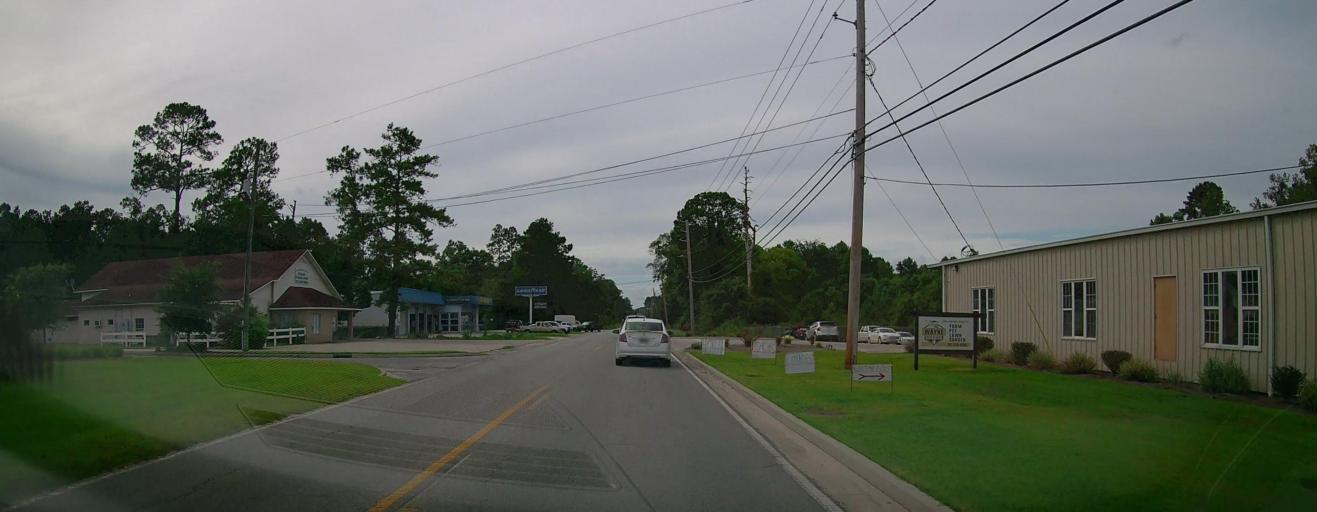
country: US
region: Georgia
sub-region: Wayne County
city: Jesup
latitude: 31.6109
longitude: -81.8897
